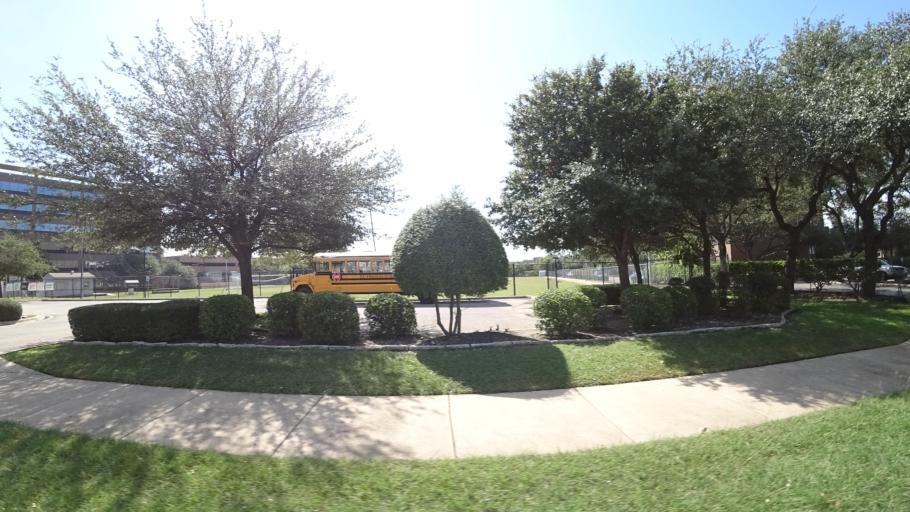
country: US
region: Texas
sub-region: Travis County
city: Austin
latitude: 30.3308
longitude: -97.7103
